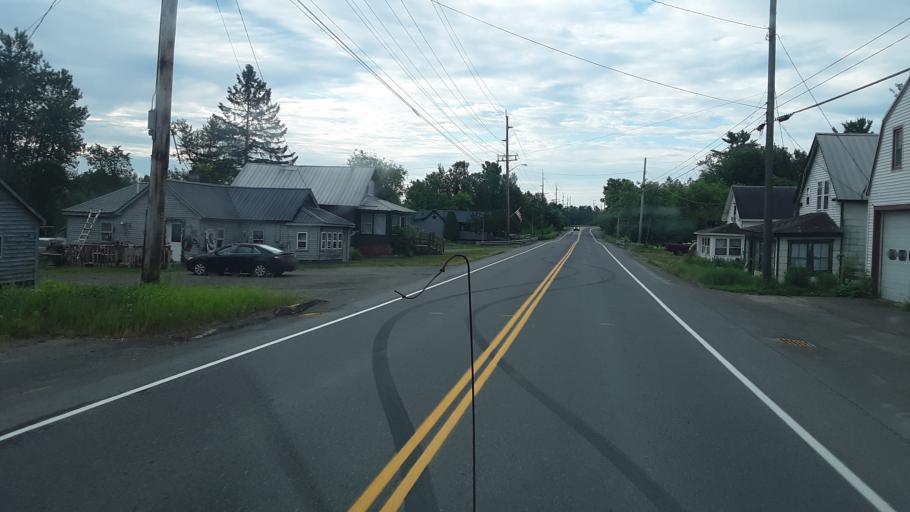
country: US
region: Maine
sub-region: Penobscot County
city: Patten
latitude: 45.8984
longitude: -68.4280
